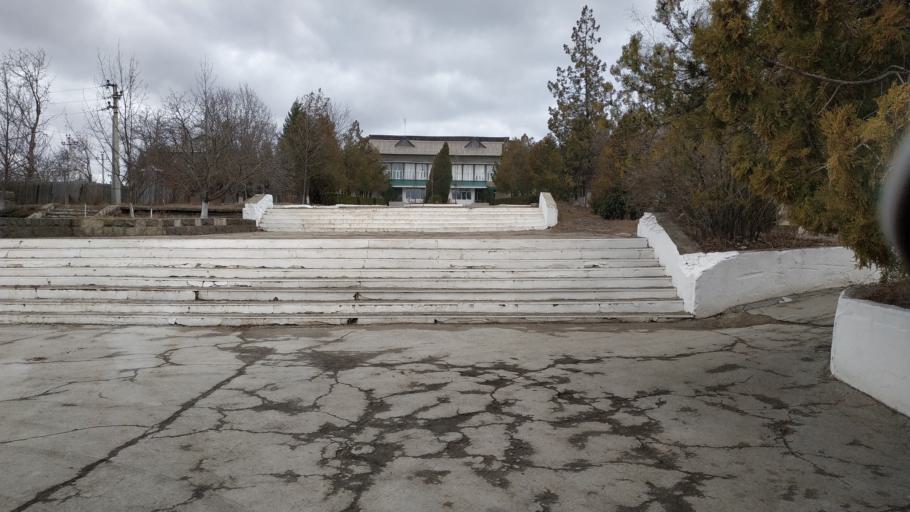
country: MD
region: Calarasi
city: Calarasi
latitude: 47.2093
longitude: 28.2538
